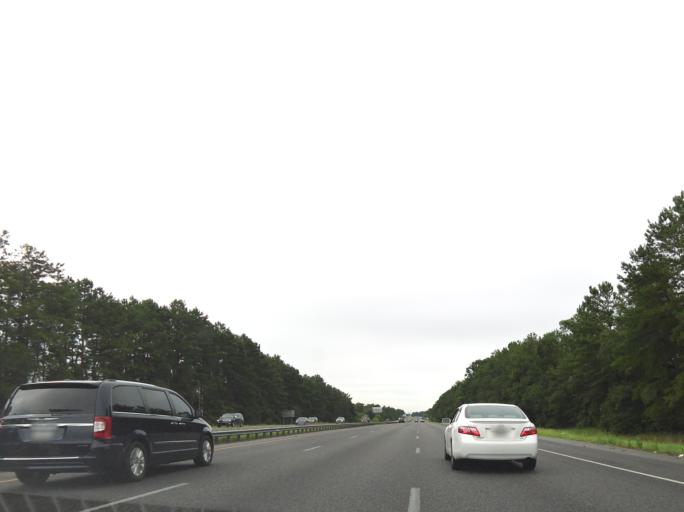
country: US
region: Georgia
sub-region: Lowndes County
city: Valdosta
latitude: 30.7855
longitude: -83.2993
